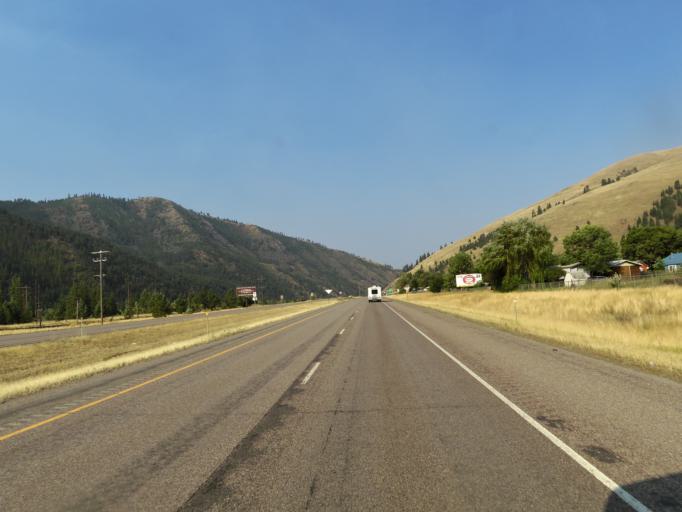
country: US
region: Montana
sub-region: Missoula County
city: East Missoula
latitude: 46.8695
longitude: -113.9404
